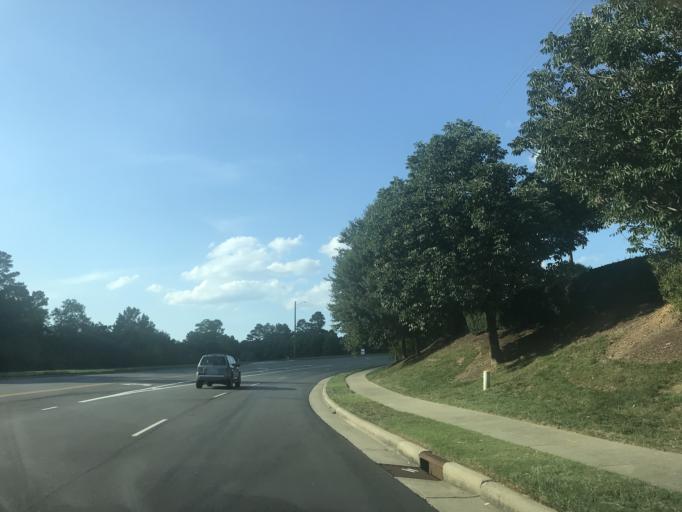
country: US
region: North Carolina
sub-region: Wake County
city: Knightdale
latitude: 35.7916
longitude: -78.5496
